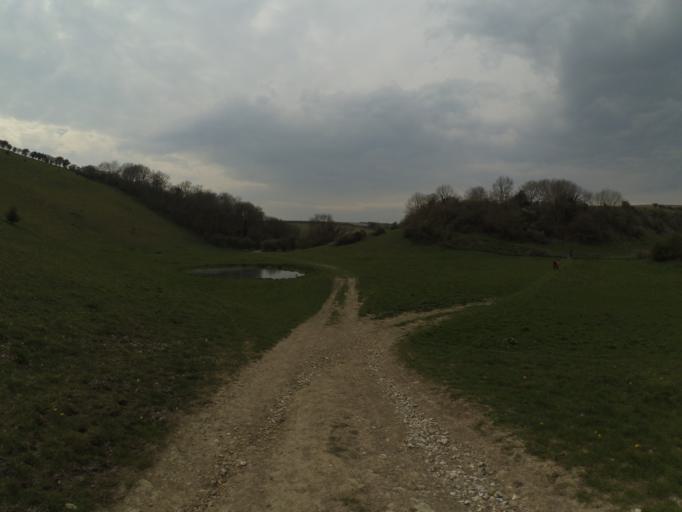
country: GB
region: England
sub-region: West Sussex
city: Arundel
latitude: 50.8942
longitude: -0.5206
